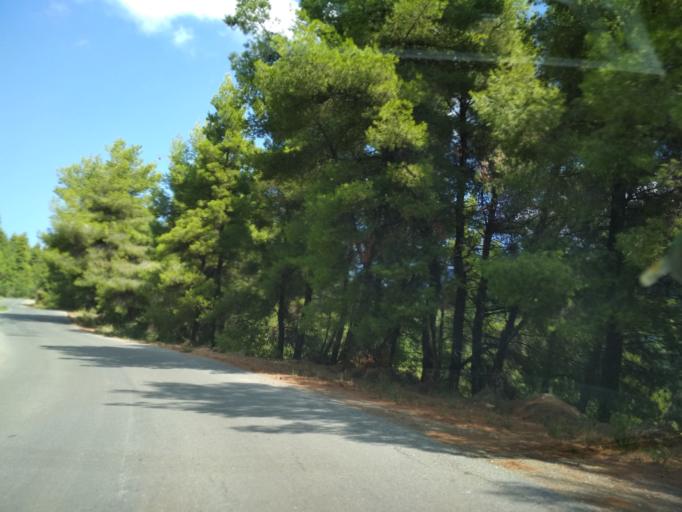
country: GR
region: Central Greece
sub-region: Nomos Evvoias
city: Roviai
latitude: 38.8350
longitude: 23.2864
